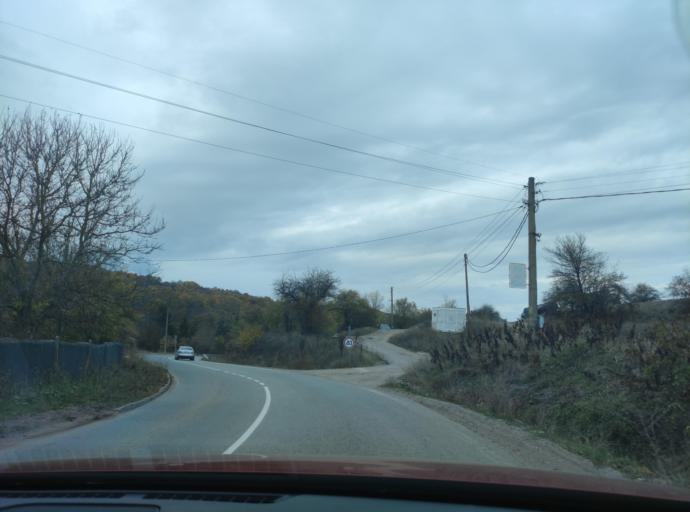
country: BG
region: Sofiya
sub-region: Obshtina Godech
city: Godech
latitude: 42.9648
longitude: 23.1553
